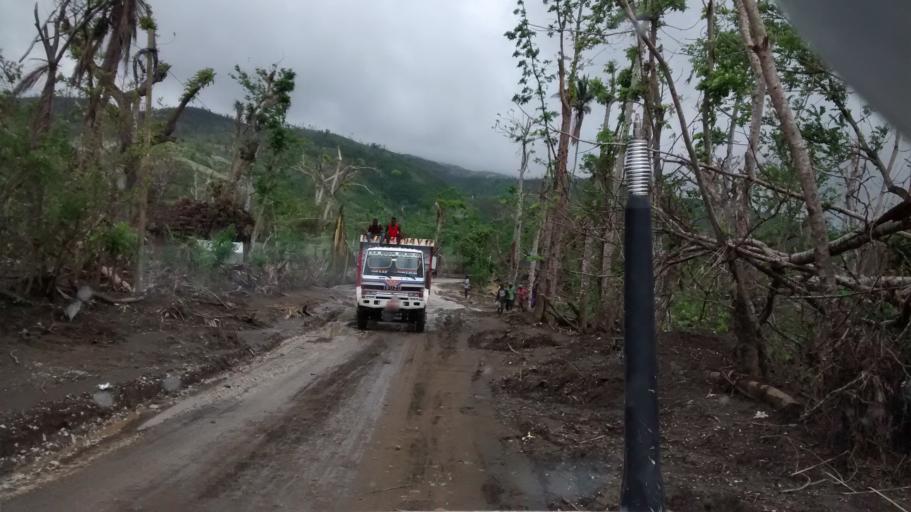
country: HT
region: Grandans
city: Moron
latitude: 18.5895
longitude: -74.2063
